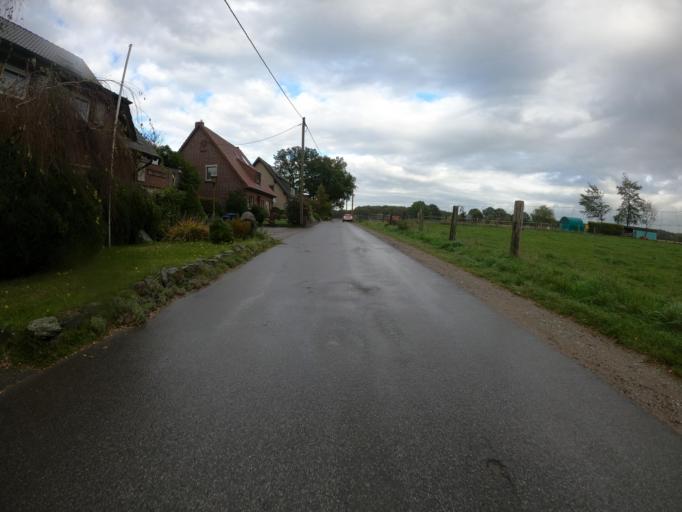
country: DE
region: North Rhine-Westphalia
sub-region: Regierungsbezirk Dusseldorf
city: Schermbeck
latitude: 51.7230
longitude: 6.8690
